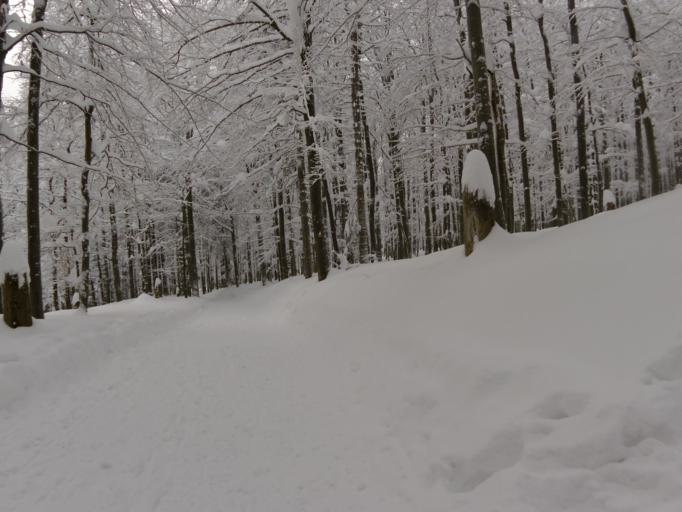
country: DE
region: Bavaria
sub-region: Lower Bavaria
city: Neuschonau
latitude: 48.9306
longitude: 13.4951
